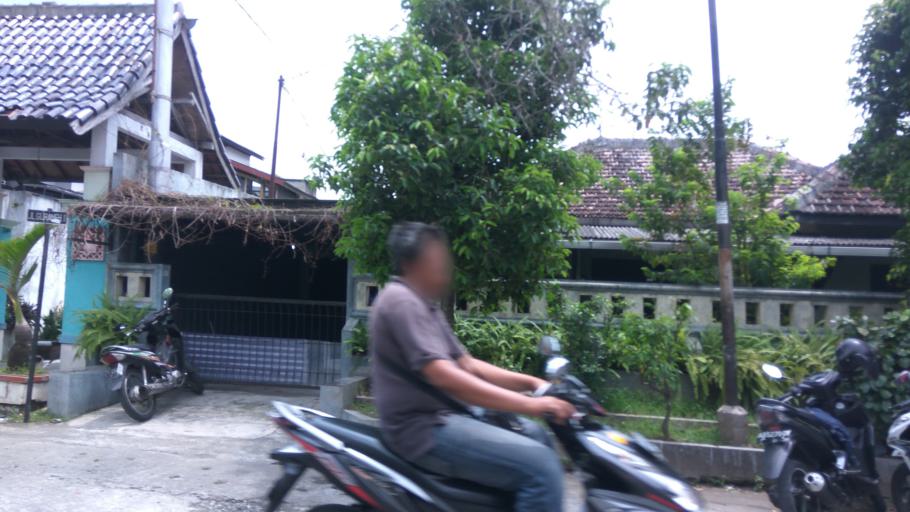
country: ID
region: Daerah Istimewa Yogyakarta
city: Depok
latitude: -7.7479
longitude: 110.4063
